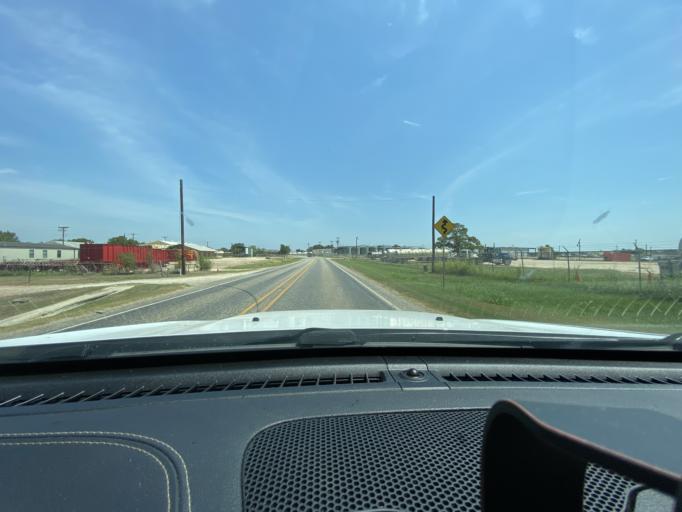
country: US
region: Texas
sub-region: Lee County
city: Giddings
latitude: 30.1665
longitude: -96.9424
